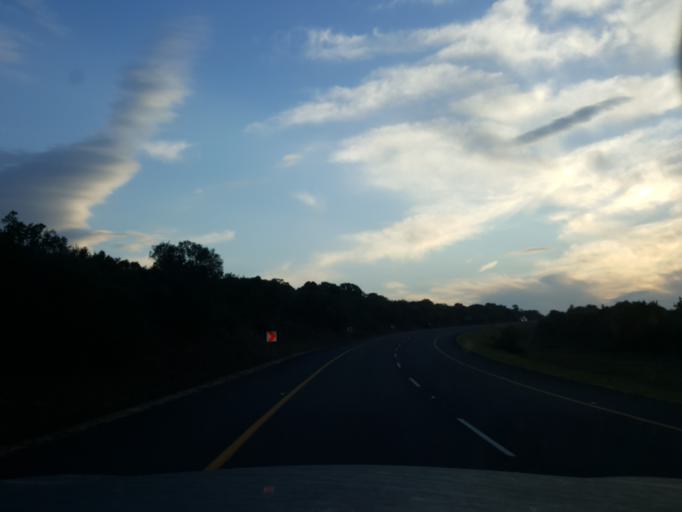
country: ZA
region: Eastern Cape
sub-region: Cacadu District Municipality
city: Grahamstown
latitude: -33.3798
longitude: 26.4616
